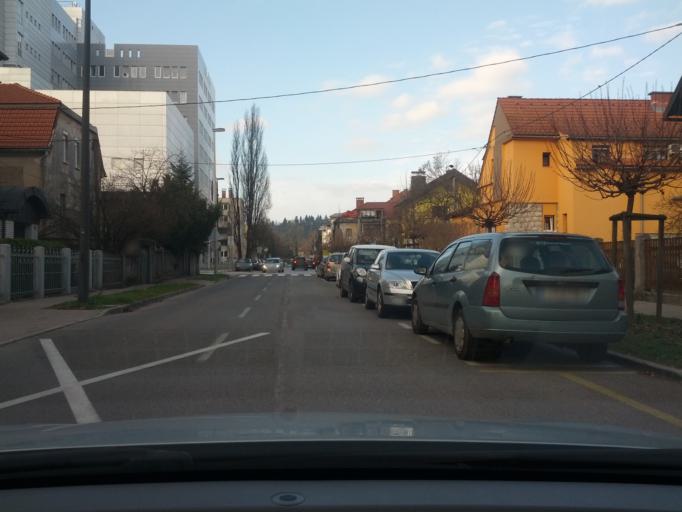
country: SI
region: Ljubljana
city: Ljubljana
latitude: 46.0451
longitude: 14.4928
